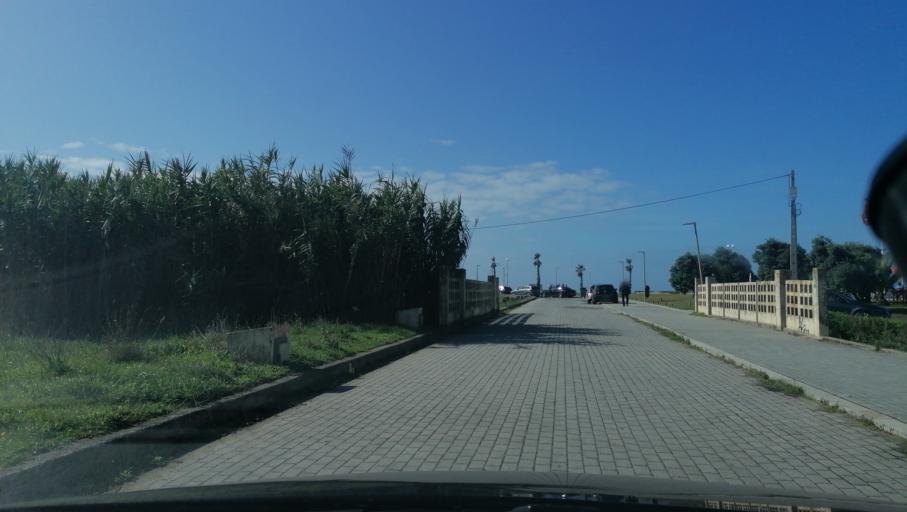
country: PT
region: Aveiro
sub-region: Espinho
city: Espinho
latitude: 41.0148
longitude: -8.6435
